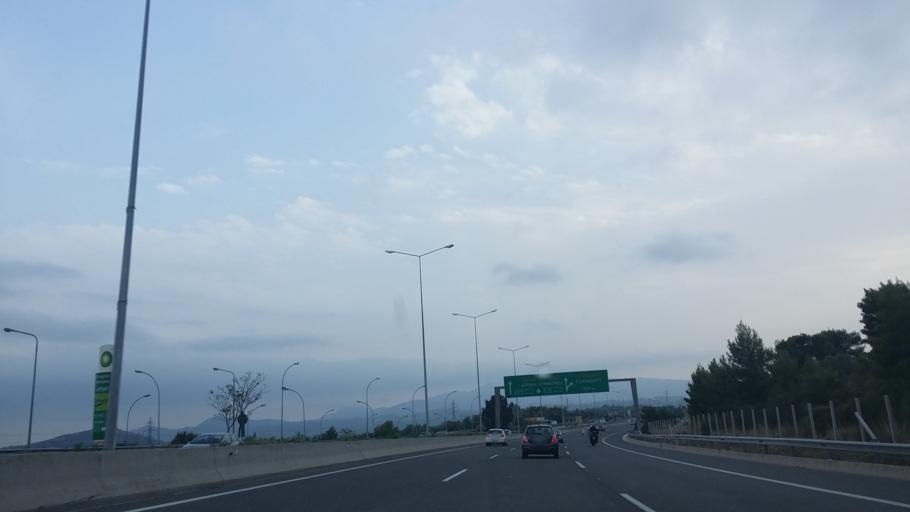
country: GR
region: Attica
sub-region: Nomarchia Anatolikis Attikis
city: Polydendri
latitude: 38.2121
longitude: 23.8549
